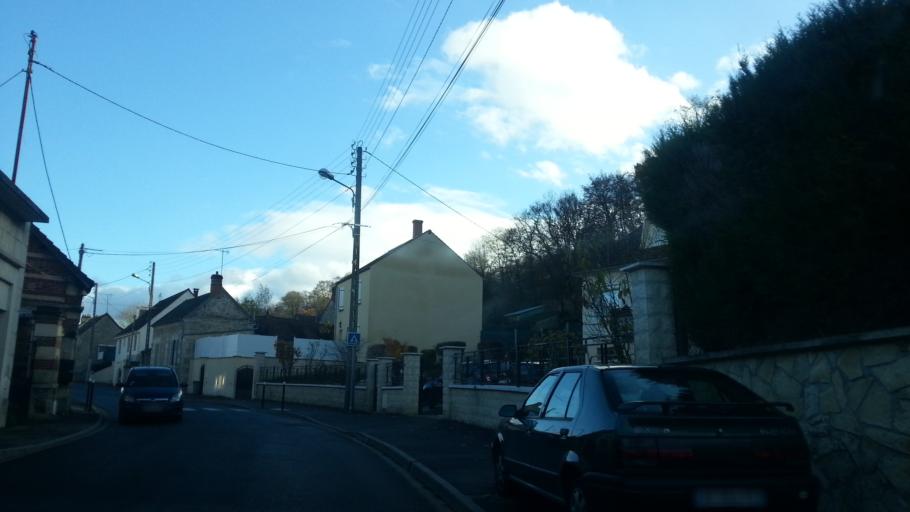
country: FR
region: Picardie
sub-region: Departement de l'Oise
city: Verneuil-en-Halatte
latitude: 49.2786
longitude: 2.5095
